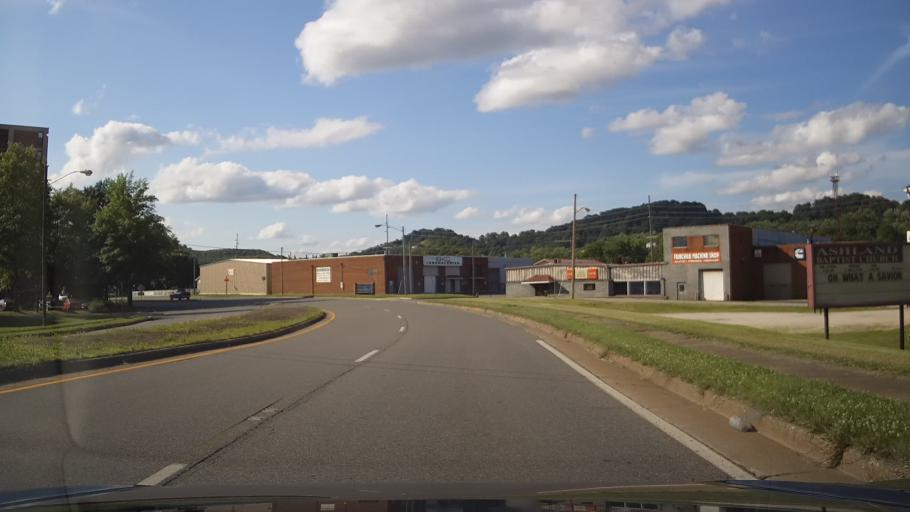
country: US
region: Kentucky
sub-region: Boyd County
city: Ashland
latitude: 38.4678
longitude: -82.6195
